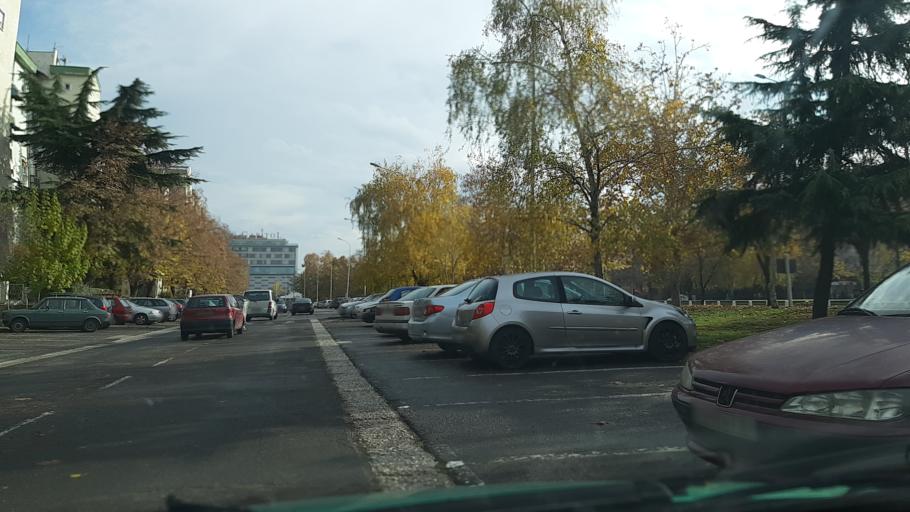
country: MK
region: Kisela Voda
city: Usje
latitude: 41.9879
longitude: 21.4630
